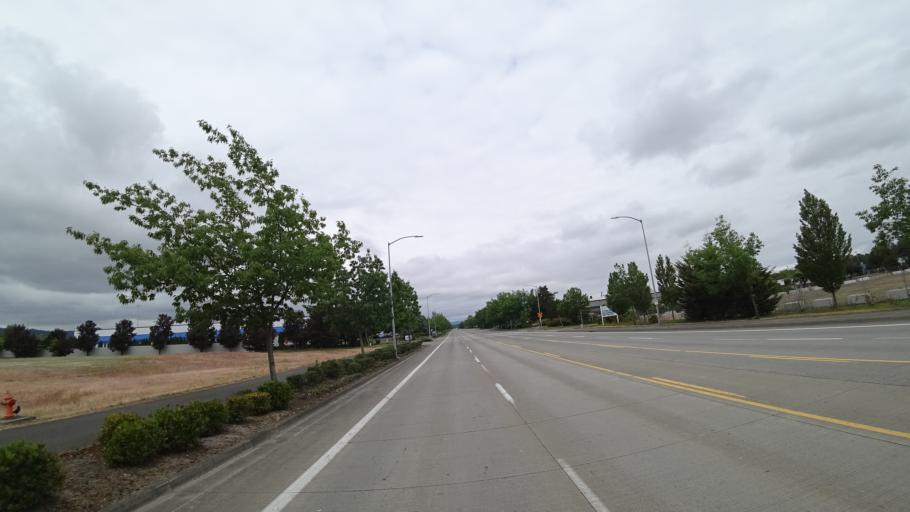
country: US
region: Washington
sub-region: Clark County
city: Vancouver
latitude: 45.6243
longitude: -122.7346
